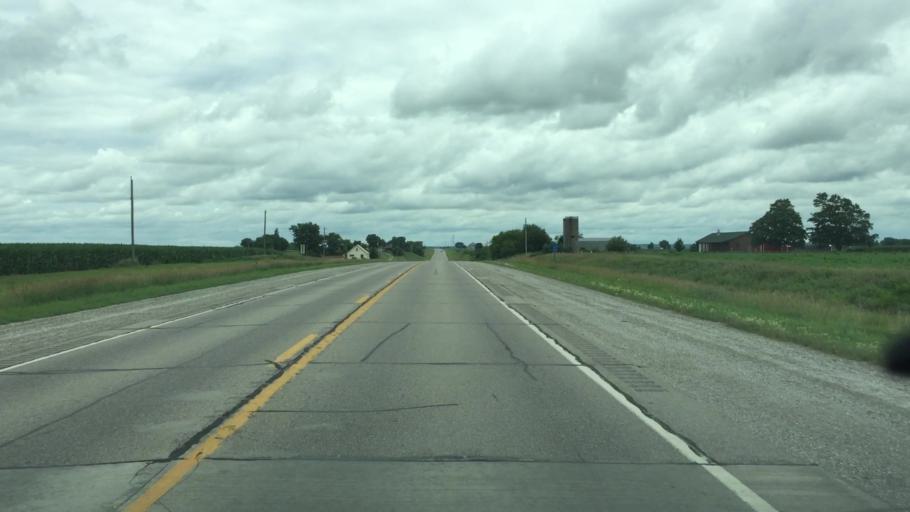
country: US
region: Iowa
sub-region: Jasper County
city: Monroe
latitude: 41.5574
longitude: -93.0971
